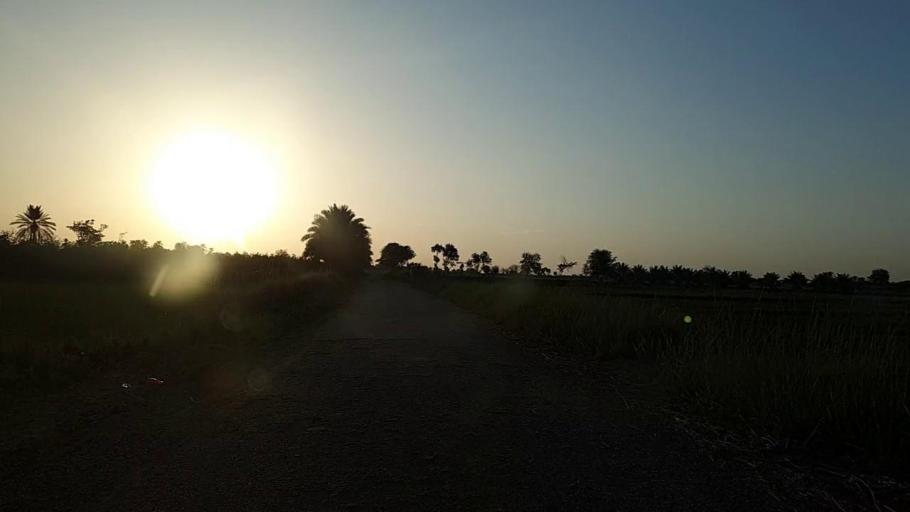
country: PK
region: Sindh
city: Hingorja
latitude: 27.0588
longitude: 68.3993
